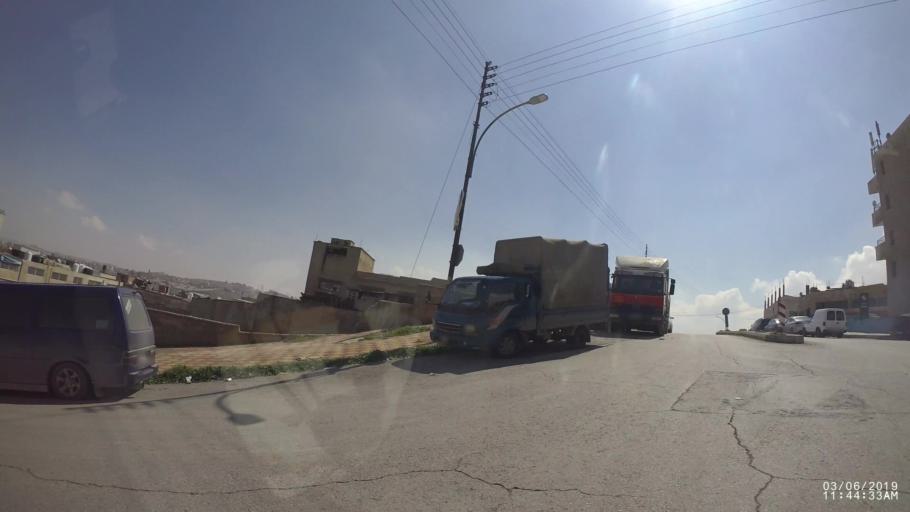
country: JO
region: Amman
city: Amman
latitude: 31.9828
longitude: 35.9976
